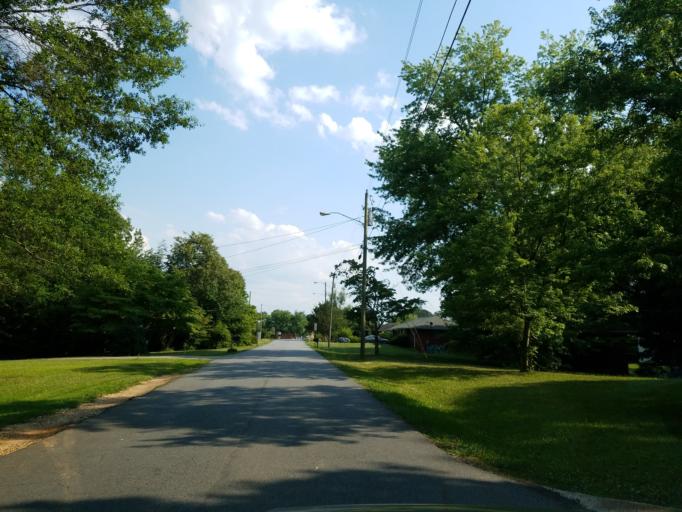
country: US
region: Georgia
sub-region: Cobb County
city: Marietta
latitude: 33.9464
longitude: -84.4810
